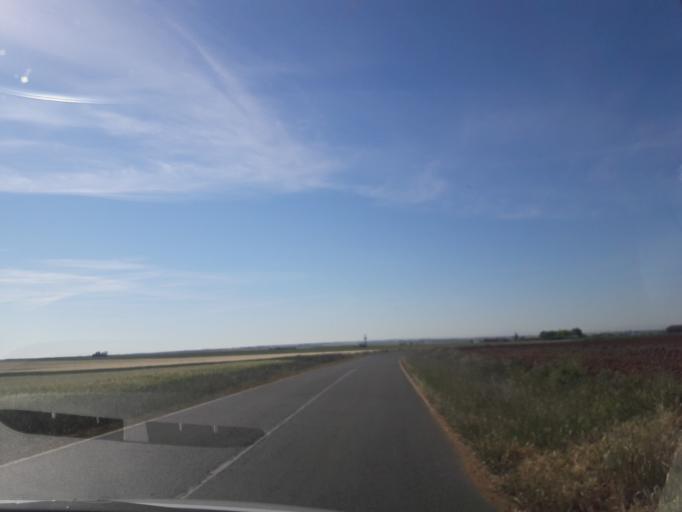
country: ES
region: Castille and Leon
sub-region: Provincia de Salamanca
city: Arcediano
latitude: 41.1028
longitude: -5.5671
